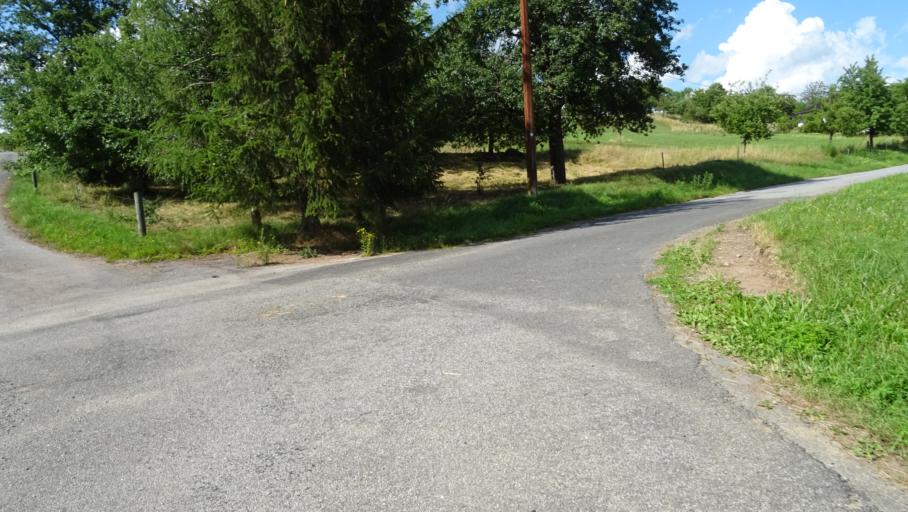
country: DE
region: Baden-Wuerttemberg
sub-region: Karlsruhe Region
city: Limbach
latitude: 49.4259
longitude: 9.2416
